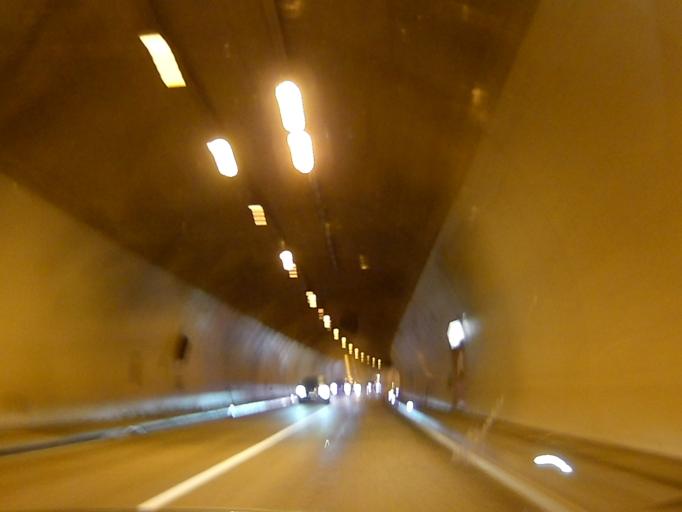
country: CH
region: Grisons
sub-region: Albula District
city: Tiefencastel
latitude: 46.6364
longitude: 9.5856
